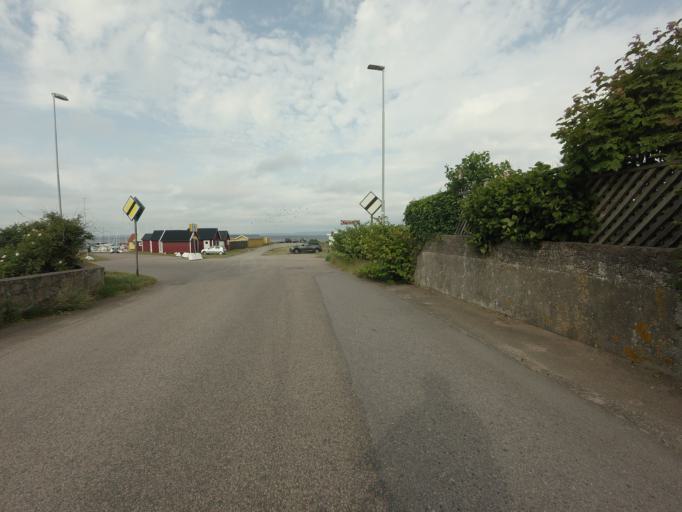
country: SE
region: Skane
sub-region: Angelholms Kommun
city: Vejbystrand
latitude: 56.3173
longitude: 12.7639
